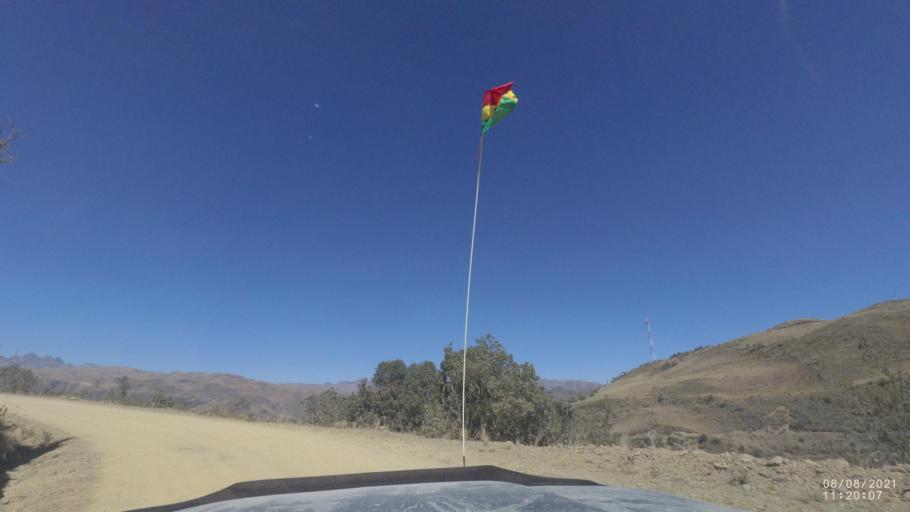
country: BO
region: Cochabamba
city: Colchani
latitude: -16.7792
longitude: -66.6613
